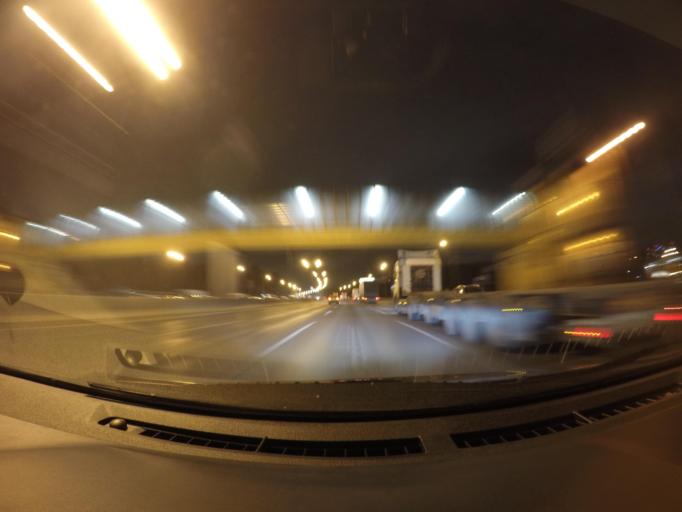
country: RU
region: Moskovskaya
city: Kotel'niki
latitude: 55.6586
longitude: 37.8398
